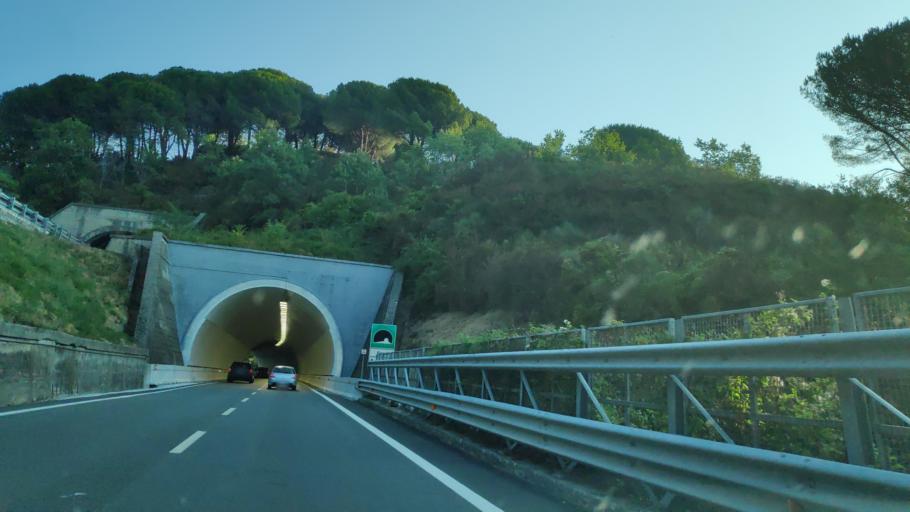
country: IT
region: Calabria
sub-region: Provincia di Cosenza
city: Belsito
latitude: 39.1714
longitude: 16.2930
